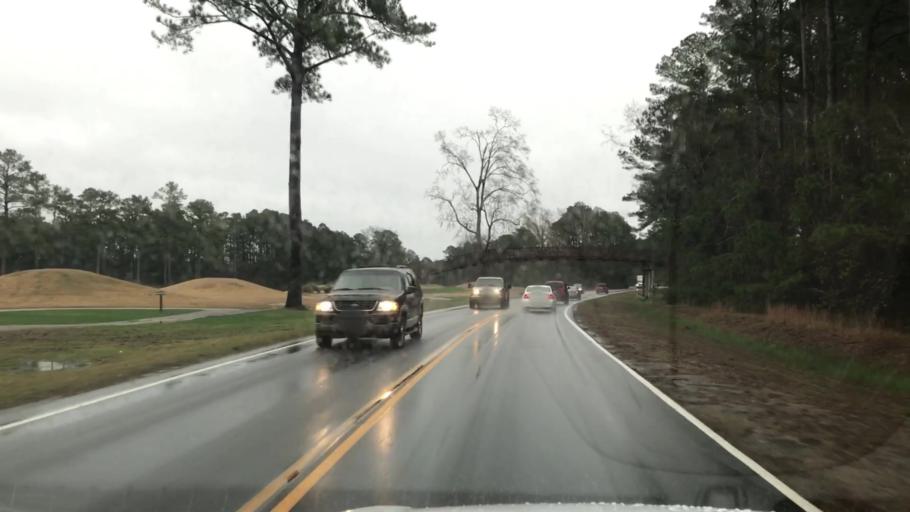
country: US
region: South Carolina
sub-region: Horry County
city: Forestbrook
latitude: 33.7274
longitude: -78.9154
